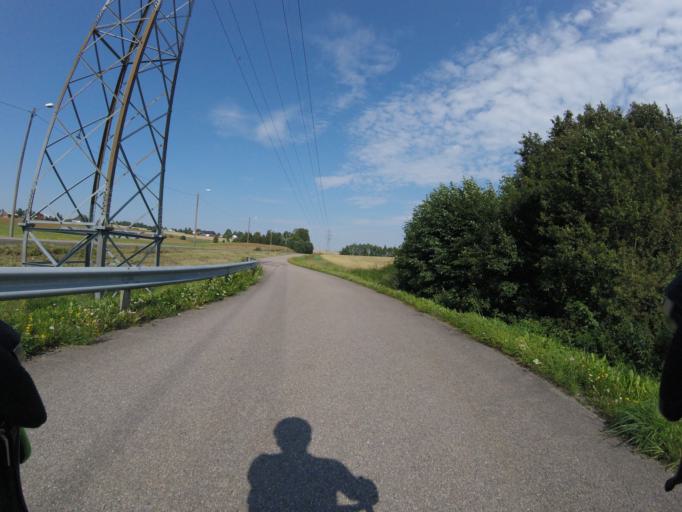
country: NO
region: Akershus
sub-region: Skedsmo
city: Leirsund
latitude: 59.9882
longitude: 11.0737
